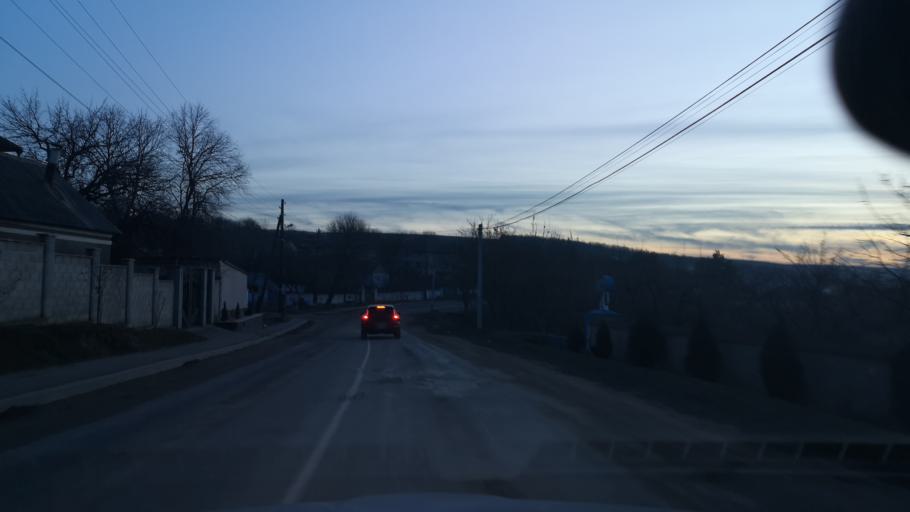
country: MD
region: Orhei
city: Orhei
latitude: 47.3074
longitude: 28.9299
